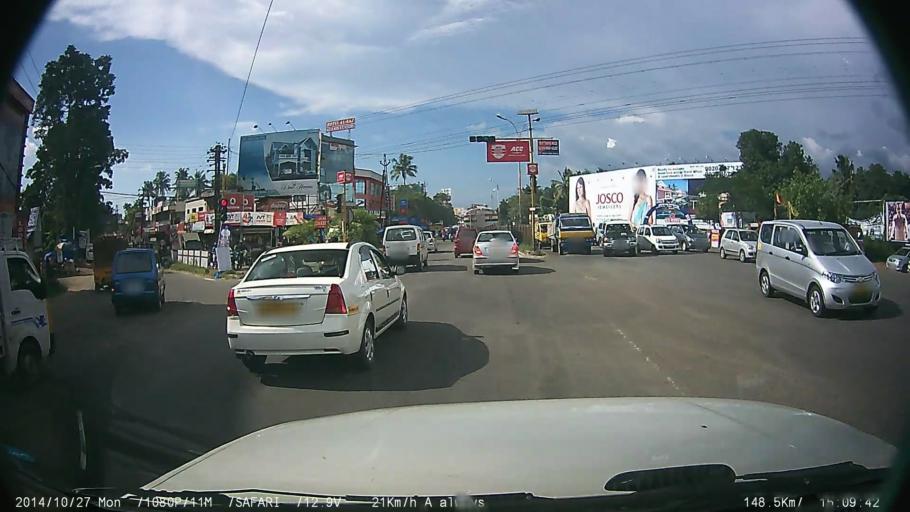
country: IN
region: Kerala
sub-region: Ernakulam
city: Aluva
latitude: 10.1194
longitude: 76.3430
